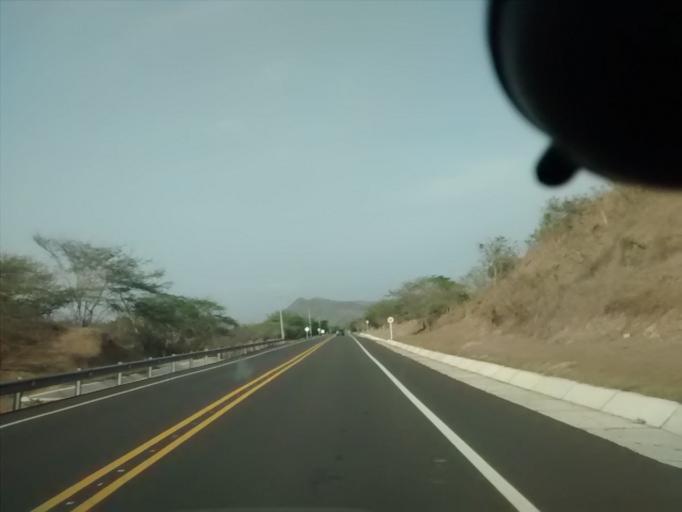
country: CO
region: Atlantico
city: Juan de Acosta
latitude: 10.8762
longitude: -75.0808
